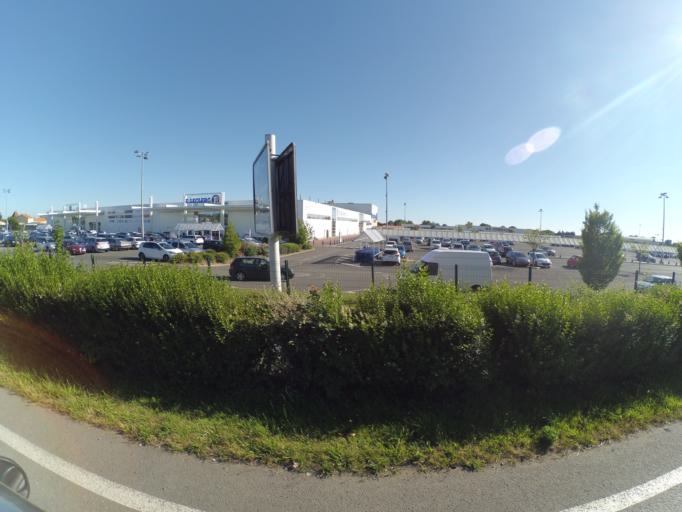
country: FR
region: Pays de la Loire
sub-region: Departement de la Vendee
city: Les Herbiers
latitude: 46.8582
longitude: -1.0135
